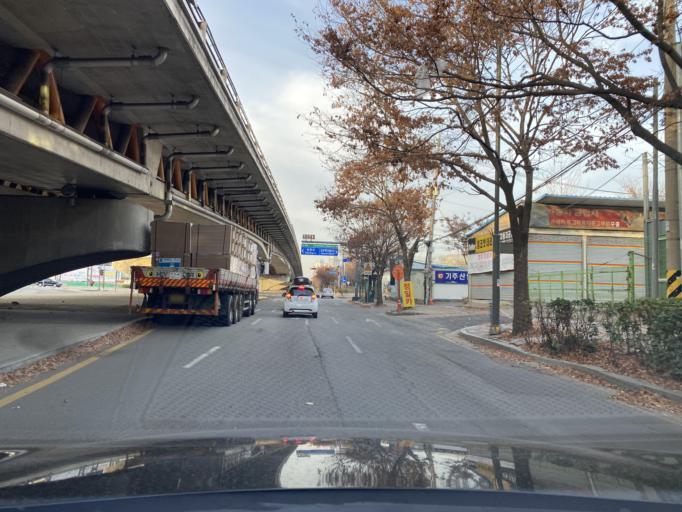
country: KR
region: Incheon
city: Incheon
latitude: 37.5057
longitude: 126.6486
